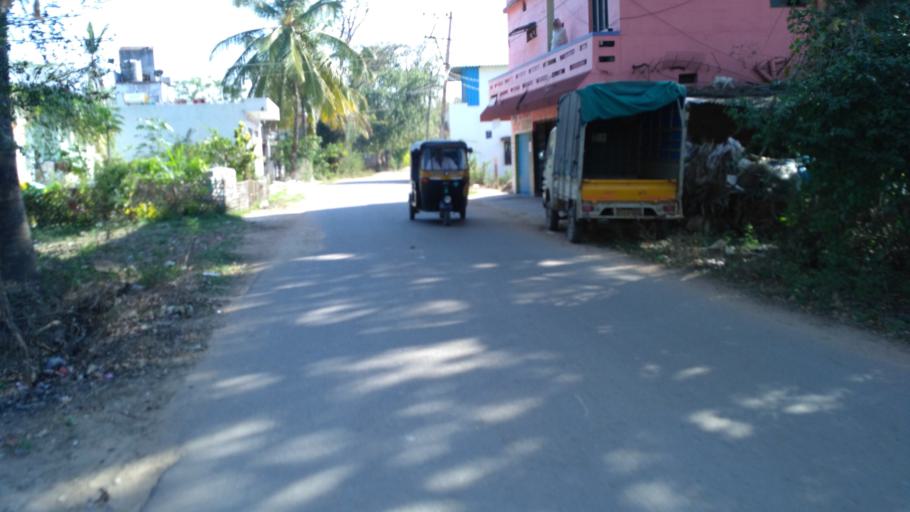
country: IN
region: Karnataka
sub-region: Hassan
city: Hassan
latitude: 13.0011
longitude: 76.1164
